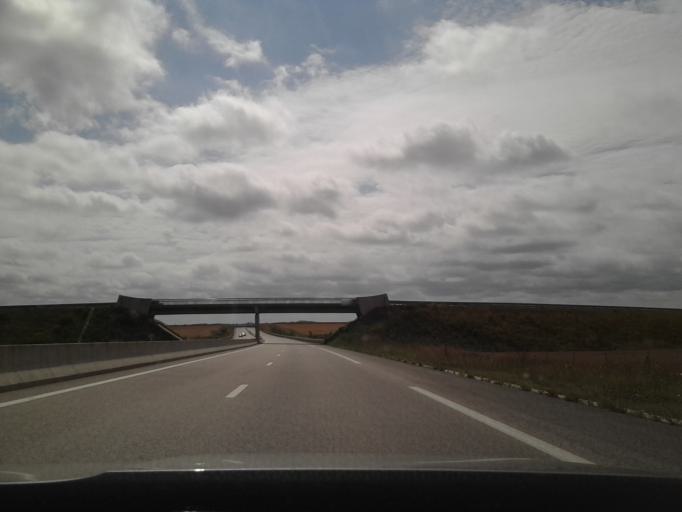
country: FR
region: Lower Normandy
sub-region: Departement de l'Orne
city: Argentan
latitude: 48.7014
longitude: -0.0411
